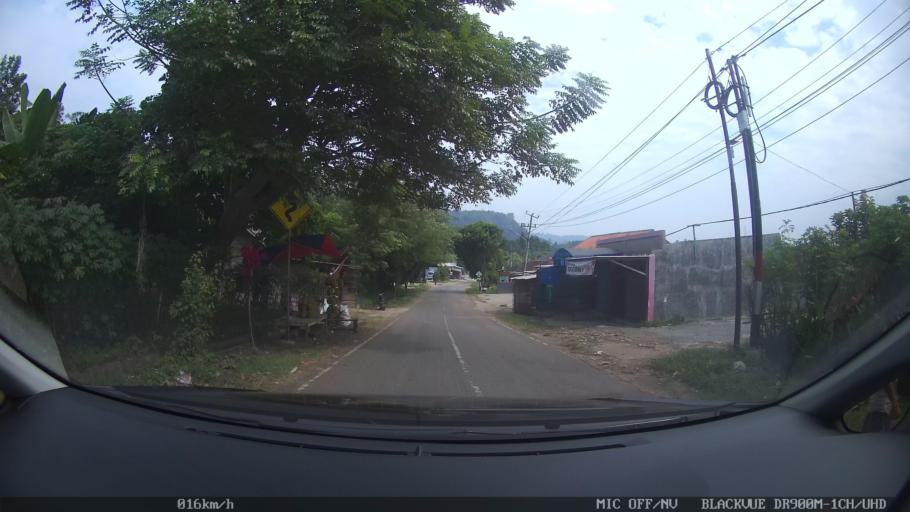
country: ID
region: Lampung
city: Bandarlampung
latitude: -5.4538
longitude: 105.2444
